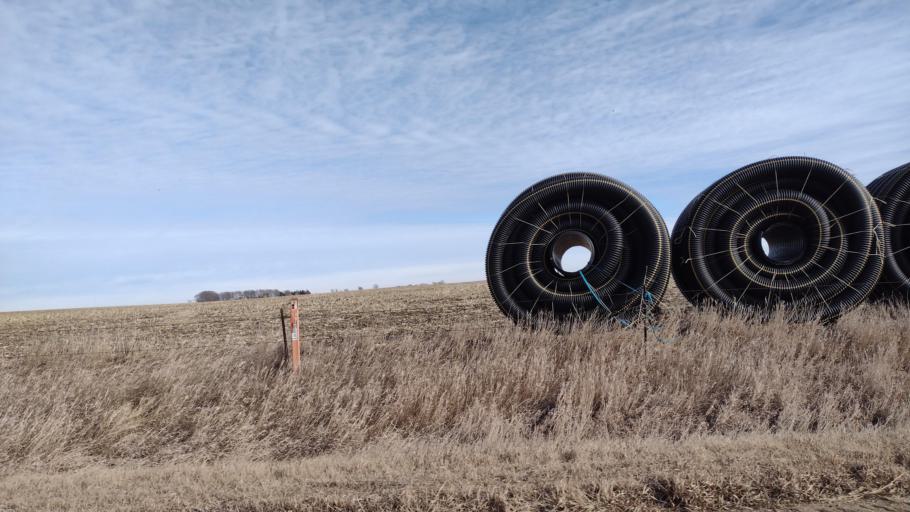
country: US
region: South Dakota
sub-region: Union County
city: Beresford
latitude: 42.9544
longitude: -96.8055
